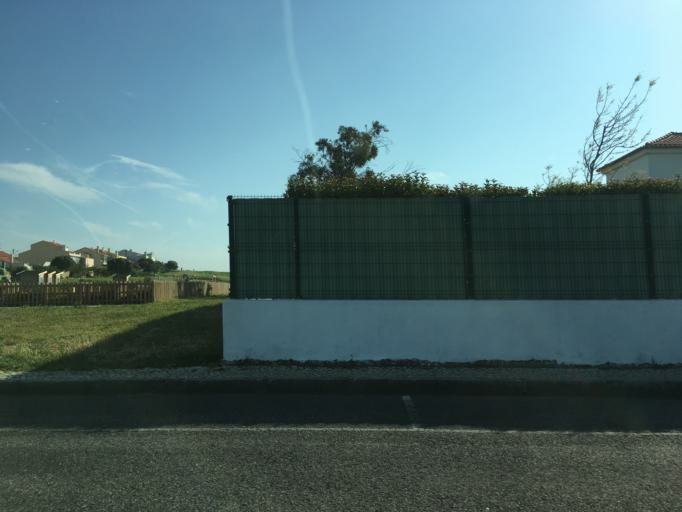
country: PT
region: Lisbon
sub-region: Cascais
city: Parede
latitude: 38.7263
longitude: -9.3540
